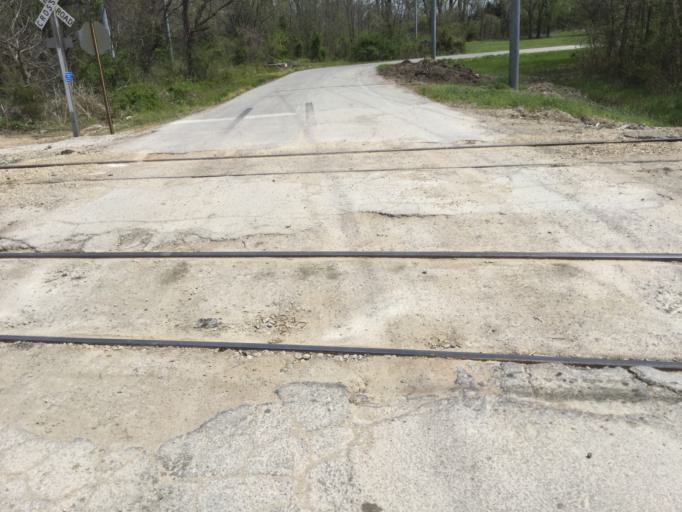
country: US
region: Kansas
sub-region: Neosho County
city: Chanute
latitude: 37.6930
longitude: -95.4501
